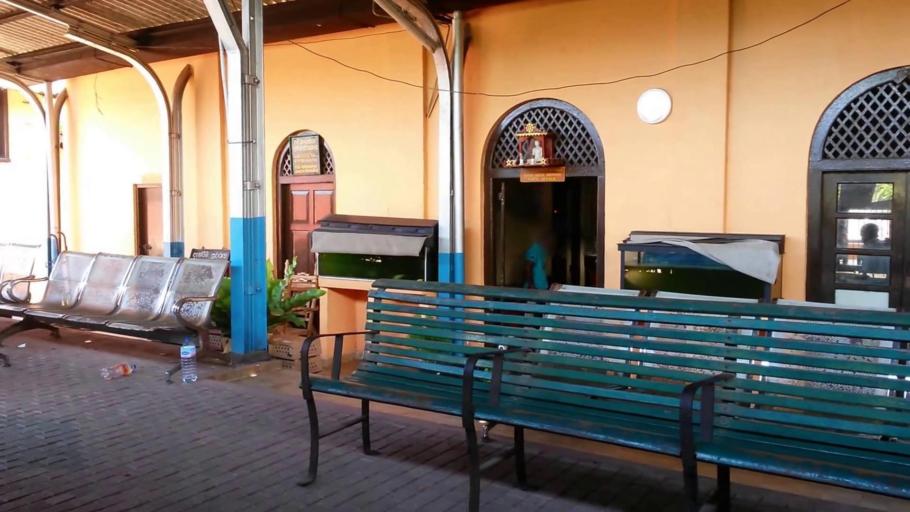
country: LK
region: Southern
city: Hikkaduwa
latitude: 6.1487
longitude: 80.0990
